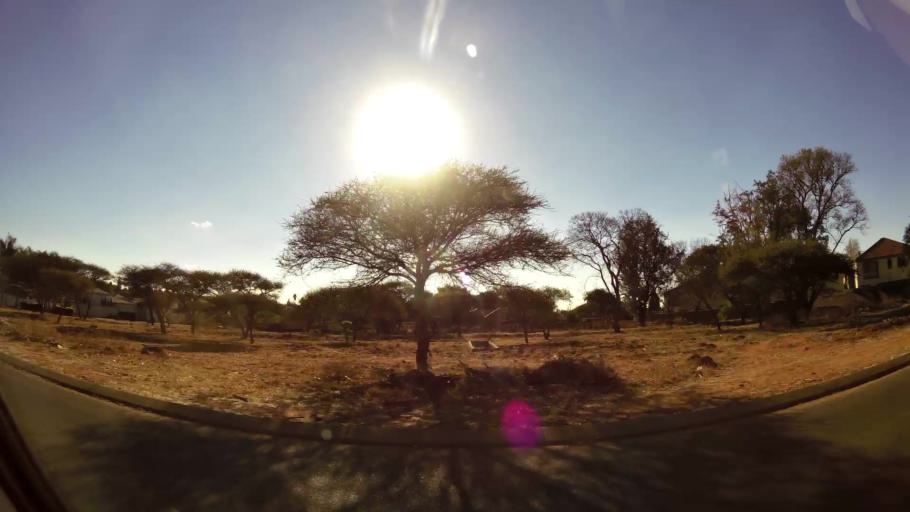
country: ZA
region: Limpopo
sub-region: Capricorn District Municipality
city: Polokwane
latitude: -23.8860
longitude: 29.4937
